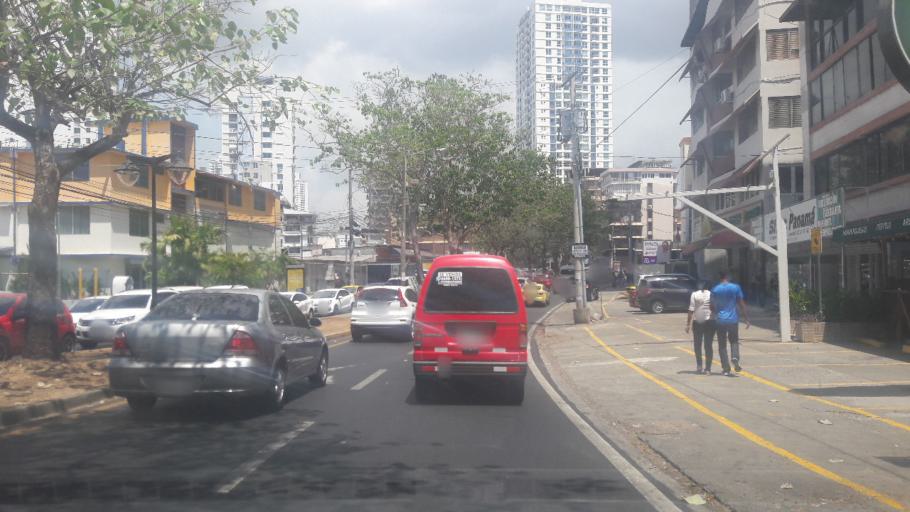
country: PA
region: Panama
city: Panama
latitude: 8.9924
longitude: -79.5224
